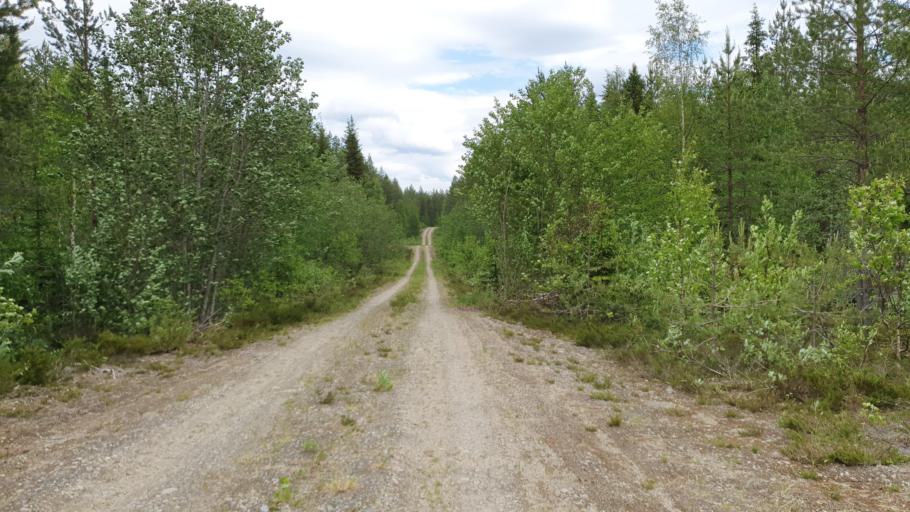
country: FI
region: Kainuu
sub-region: Kehys-Kainuu
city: Kuhmo
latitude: 64.4402
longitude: 29.6916
